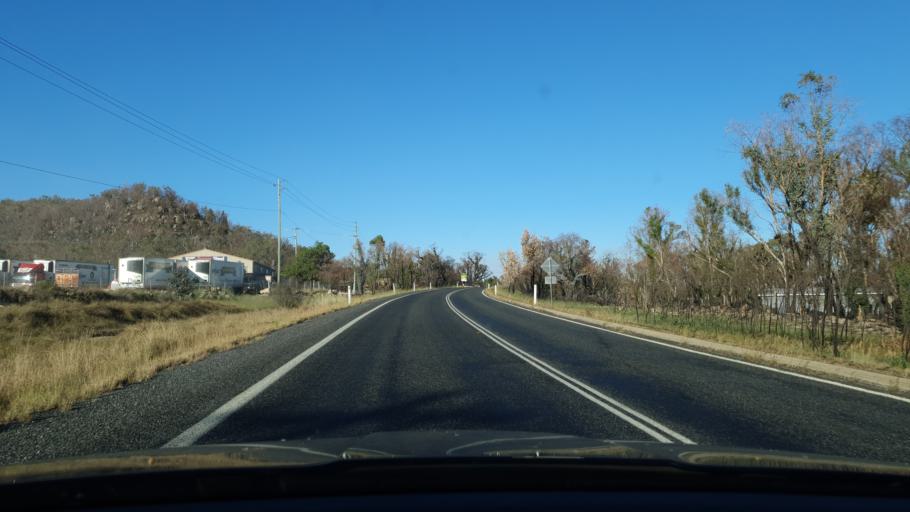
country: AU
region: Queensland
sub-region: Southern Downs
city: Stanthorpe
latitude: -28.6522
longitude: 151.9193
